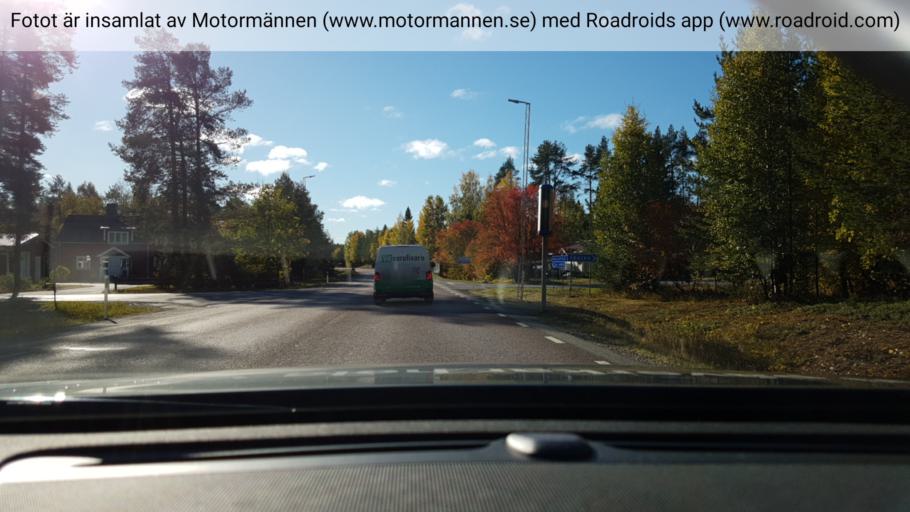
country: SE
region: Vaesterbotten
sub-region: Skelleftea Kommun
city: Burea
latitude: 64.6199
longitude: 21.1784
